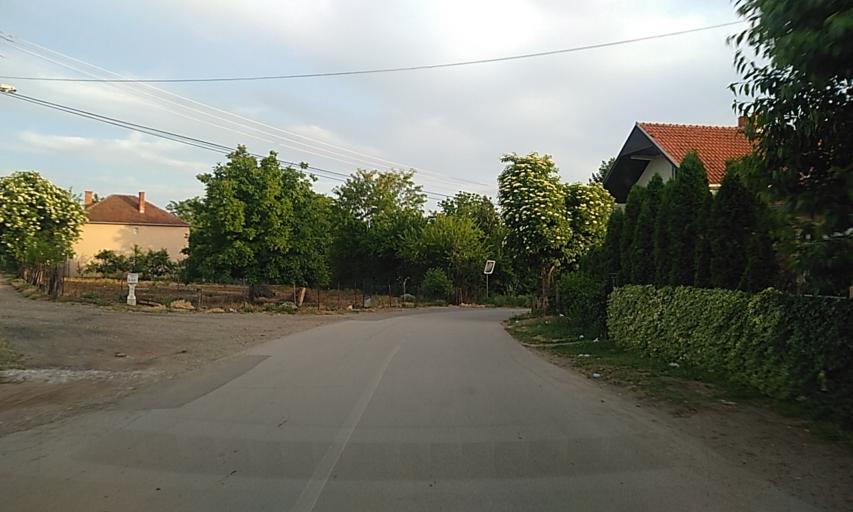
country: RS
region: Central Serbia
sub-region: Nisavski Okrug
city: Nis
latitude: 43.2949
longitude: 21.8657
